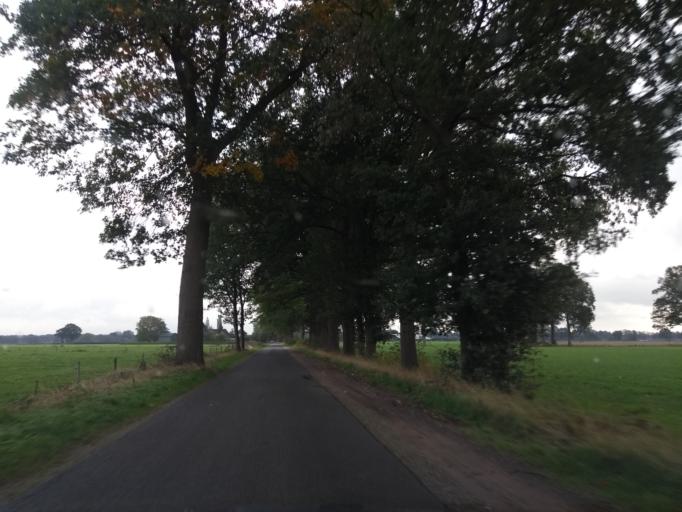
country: NL
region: Gelderland
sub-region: Gemeente Bronckhorst
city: Zelhem
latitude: 52.0187
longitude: 6.3733
